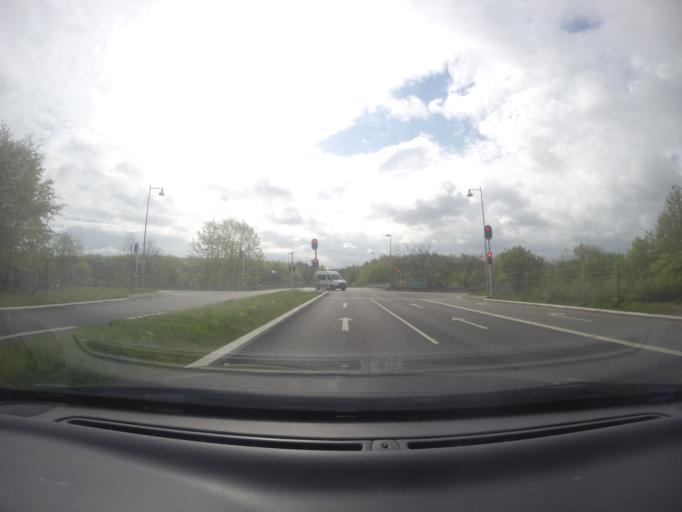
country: DK
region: Capital Region
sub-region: Albertslund Kommune
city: Albertslund
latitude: 55.6837
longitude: 12.3334
